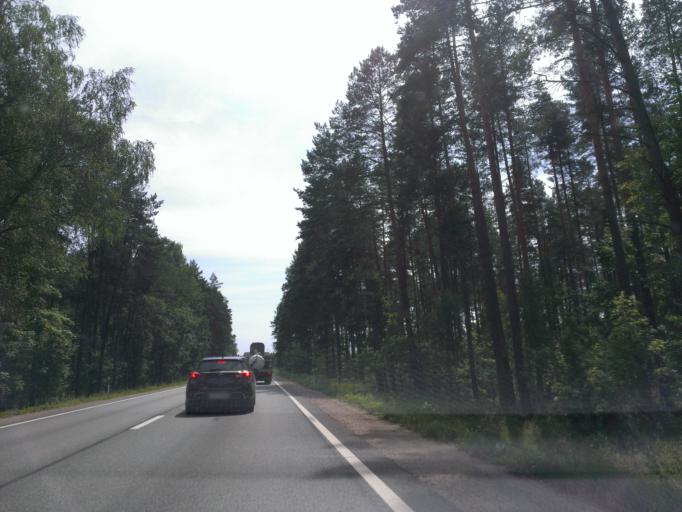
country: LV
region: Salaspils
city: Salaspils
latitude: 56.9468
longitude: 24.3803
